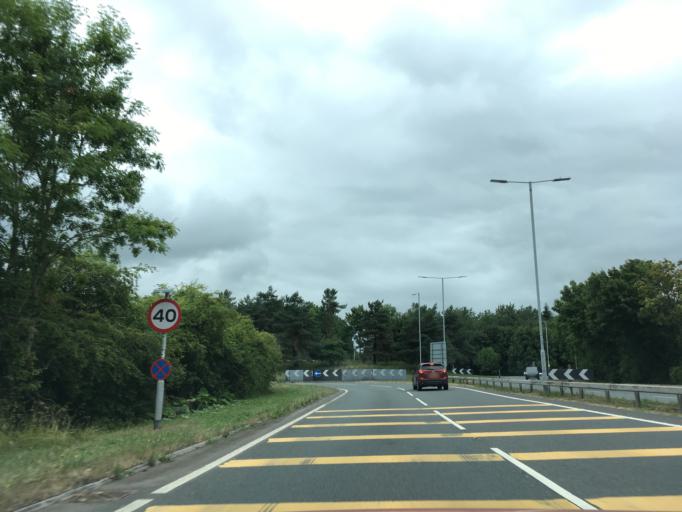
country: GB
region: Wales
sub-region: Sir Powys
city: Brecon
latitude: 51.9447
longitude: -3.4089
